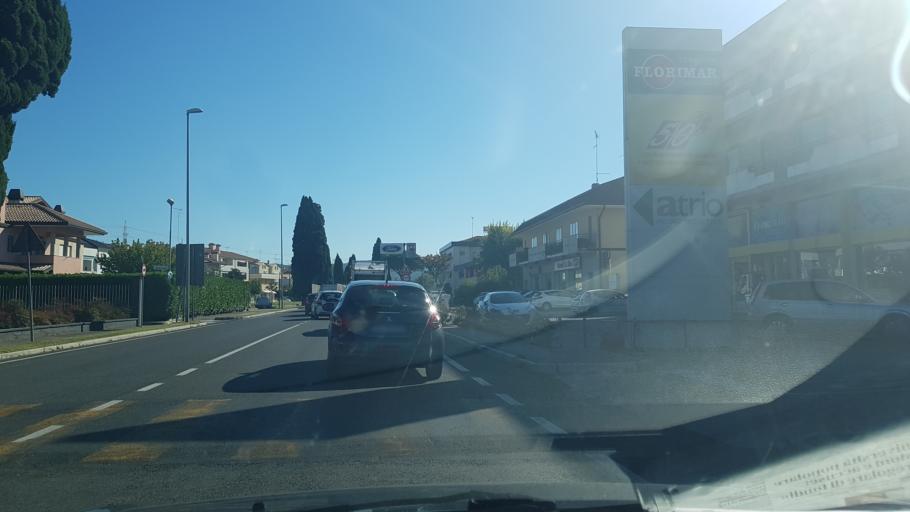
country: IT
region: Friuli Venezia Giulia
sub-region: Provincia di Gorizia
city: Monfalcone
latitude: 45.8017
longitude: 13.5532
